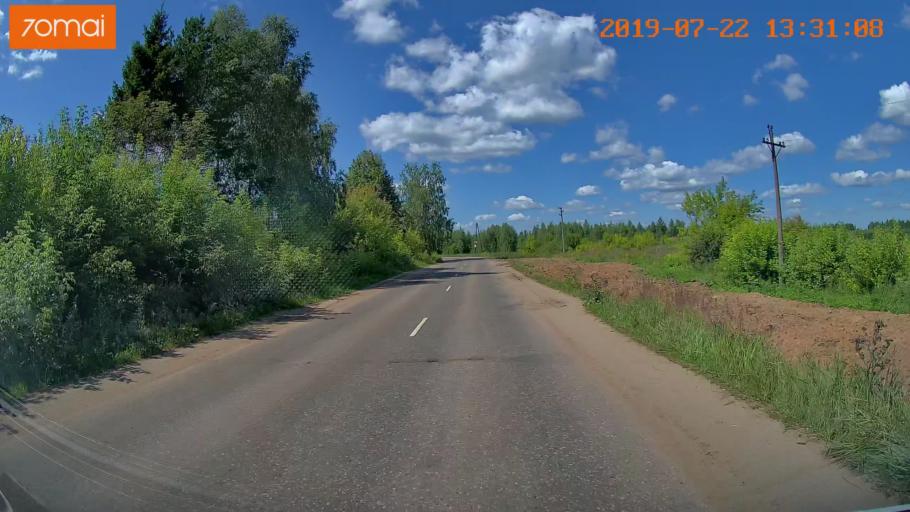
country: RU
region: Ivanovo
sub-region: Gorod Ivanovo
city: Ivanovo
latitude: 57.0564
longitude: 40.9199
